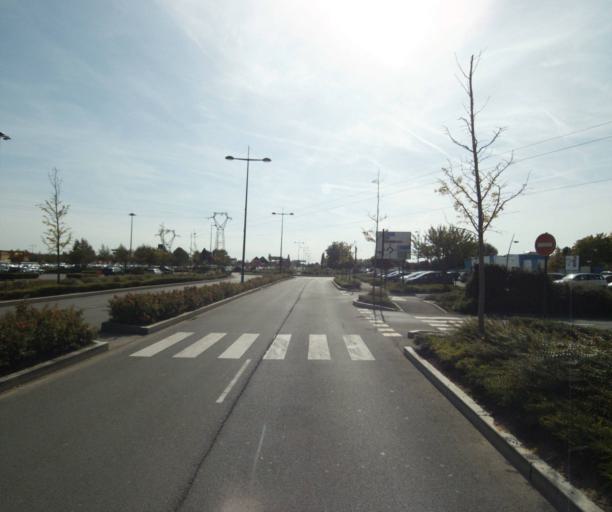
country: FR
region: Nord-Pas-de-Calais
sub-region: Departement du Nord
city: Capinghem
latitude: 50.6317
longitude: 2.9654
